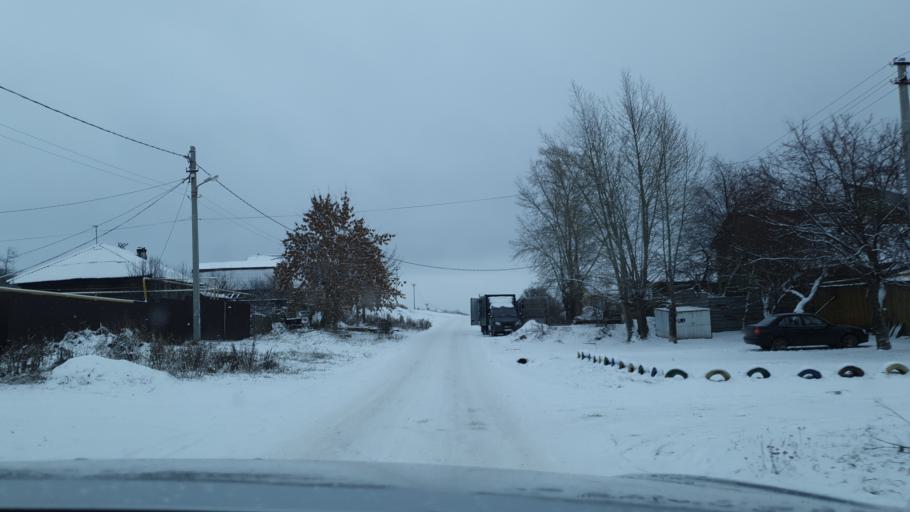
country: RU
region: Sverdlovsk
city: Istok
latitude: 56.7442
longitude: 60.6998
